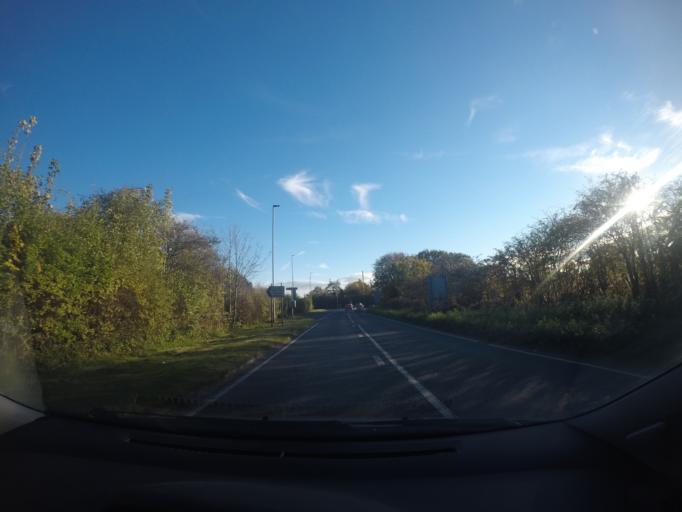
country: GB
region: England
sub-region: City of York
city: York
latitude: 53.9796
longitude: -1.0814
